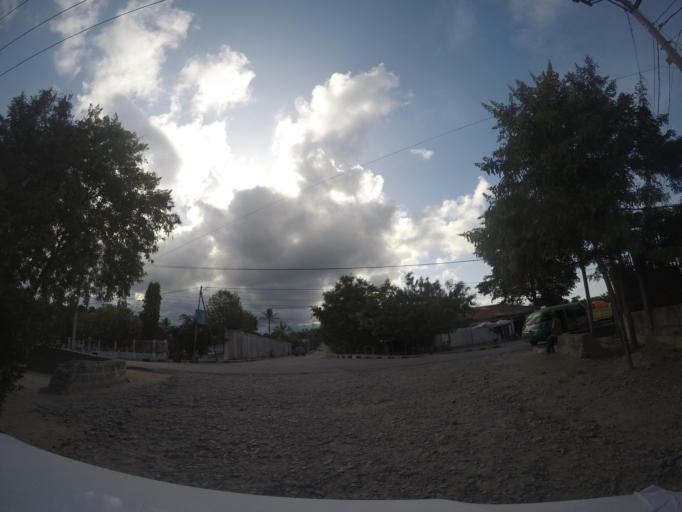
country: TL
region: Baucau
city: Baucau
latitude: -8.4762
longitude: 126.4585
